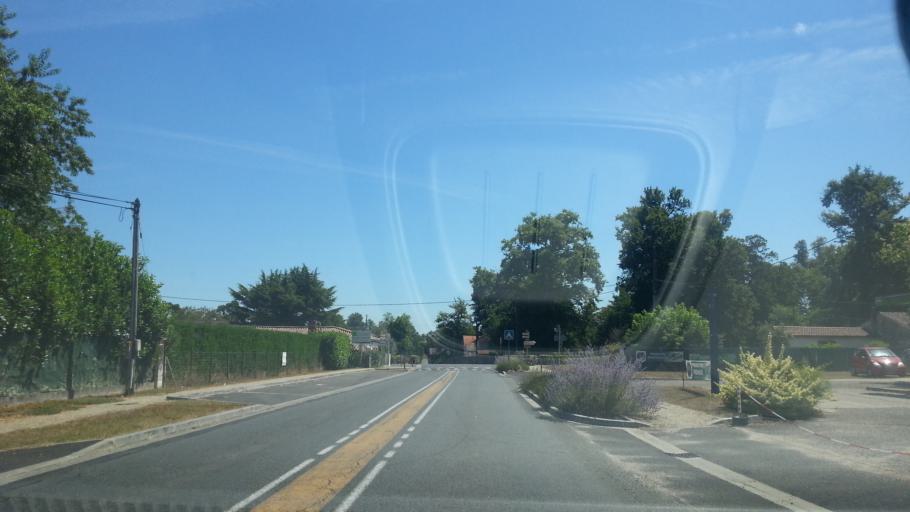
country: FR
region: Aquitaine
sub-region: Departement de la Gironde
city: Illats
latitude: 44.5600
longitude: -0.3600
